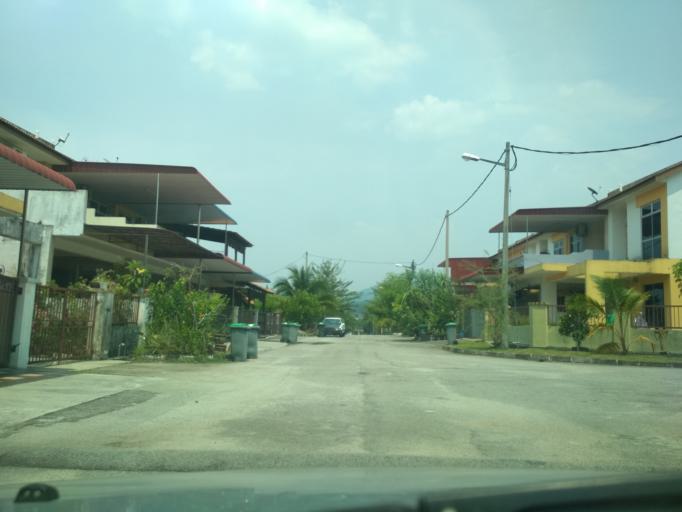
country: MY
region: Kedah
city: Kulim
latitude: 5.3600
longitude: 100.5354
